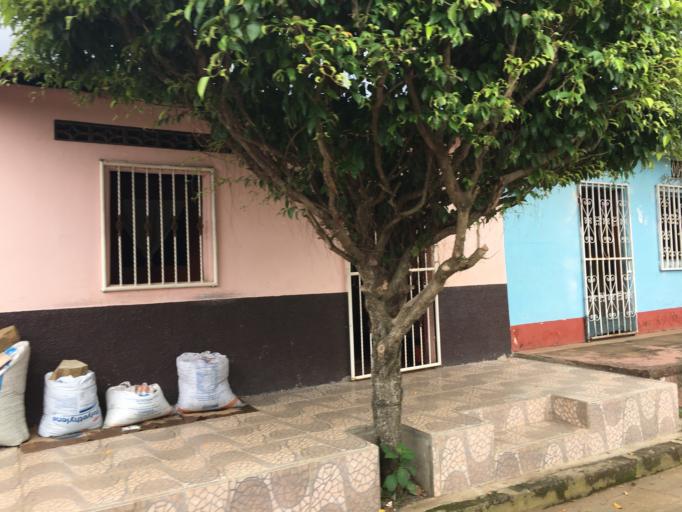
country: NI
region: Masaya
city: Masaya
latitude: 11.9824
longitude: -86.0940
